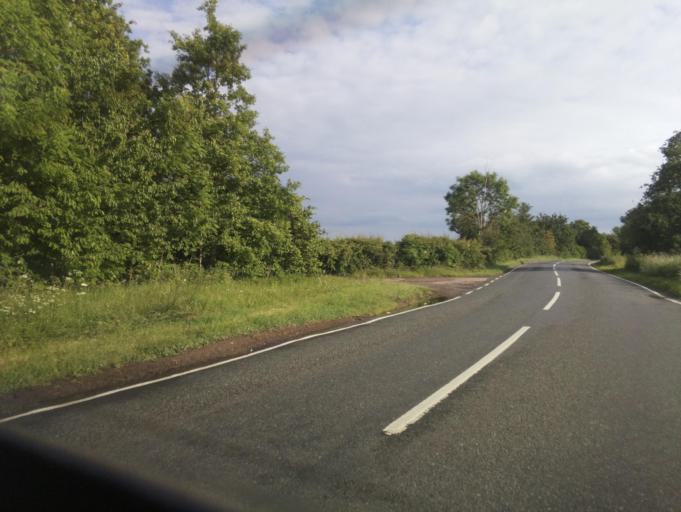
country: GB
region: England
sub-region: Lincolnshire
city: Great Gonerby
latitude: 53.0512
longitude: -0.6449
